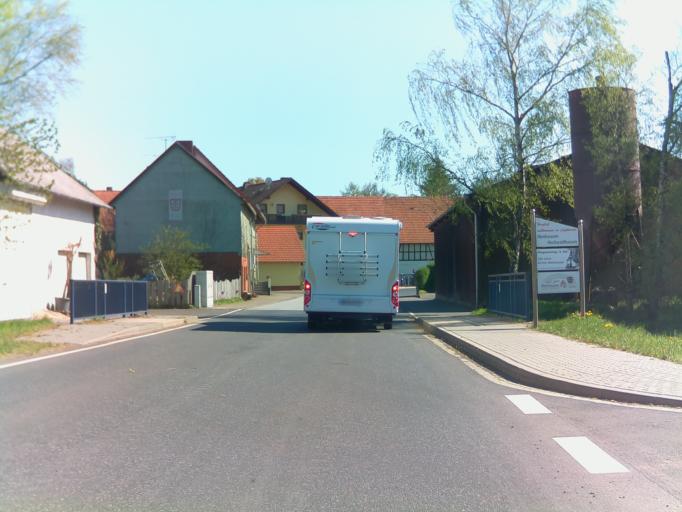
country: DE
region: Hesse
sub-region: Regierungsbezirk Giessen
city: Grebenhain
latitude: 50.5240
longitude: 9.3338
